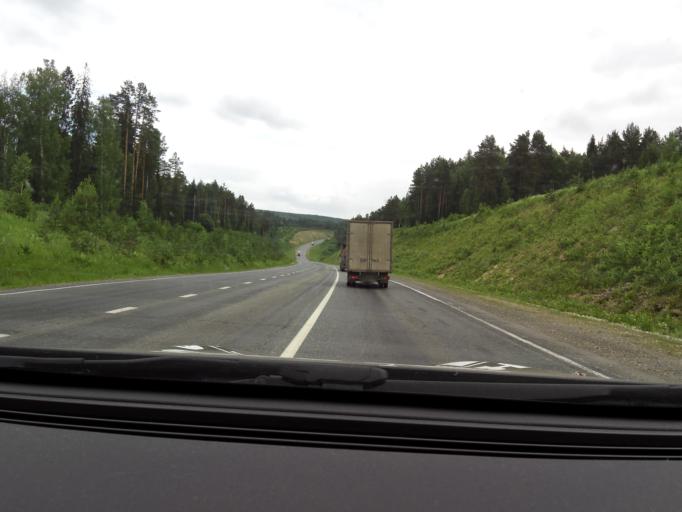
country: RU
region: Perm
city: Suksun
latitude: 57.1270
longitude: 57.3024
